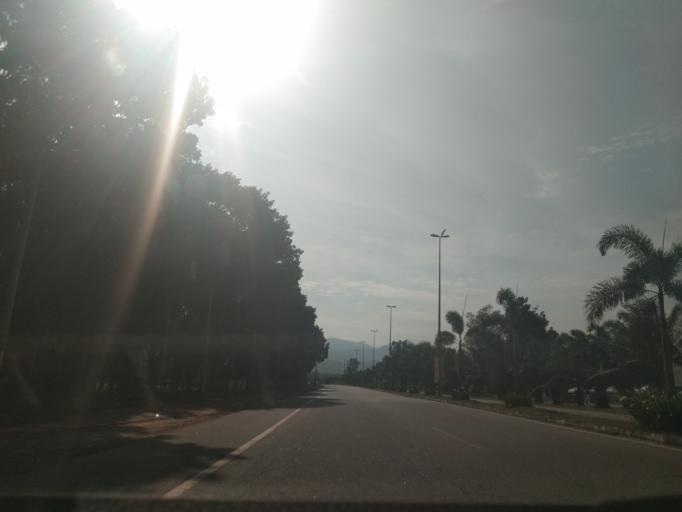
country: MY
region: Perak
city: Ipoh
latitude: 4.5010
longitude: 101.1394
